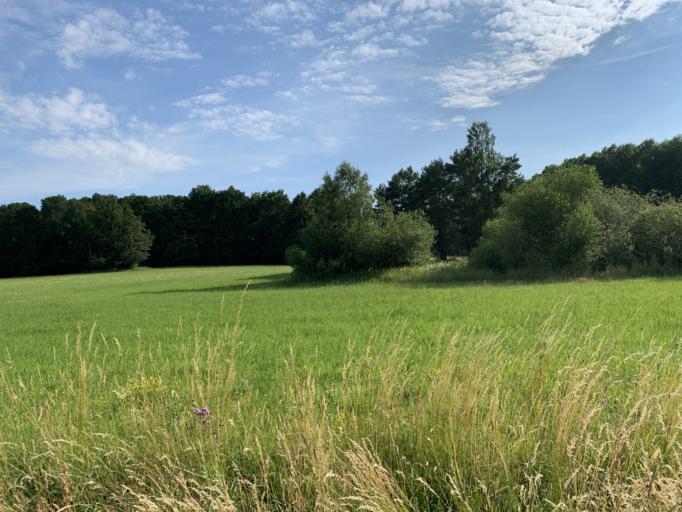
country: SE
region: Stockholm
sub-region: Jarfalla Kommun
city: Jakobsberg
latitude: 59.4423
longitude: 17.8584
